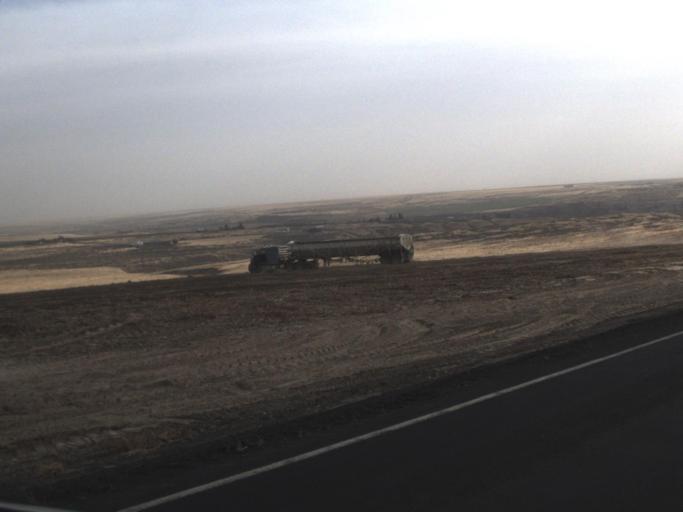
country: US
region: Washington
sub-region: Adams County
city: Ritzville
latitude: 47.3601
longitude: -118.6995
